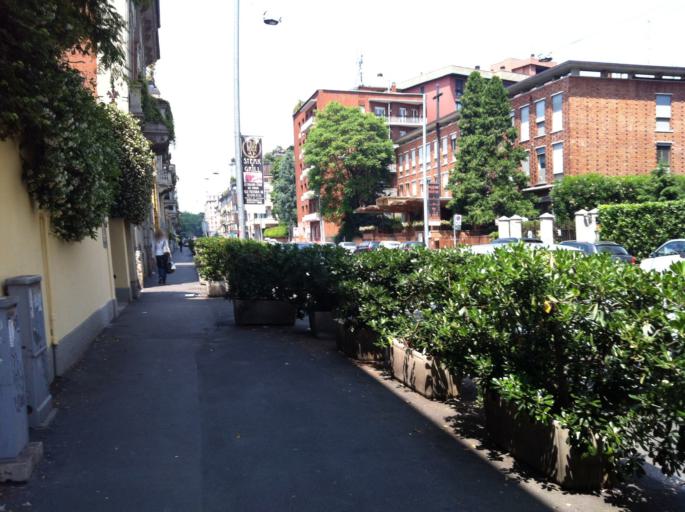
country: IT
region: Lombardy
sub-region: Citta metropolitana di Milano
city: Milano
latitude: 45.4710
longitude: 9.2112
